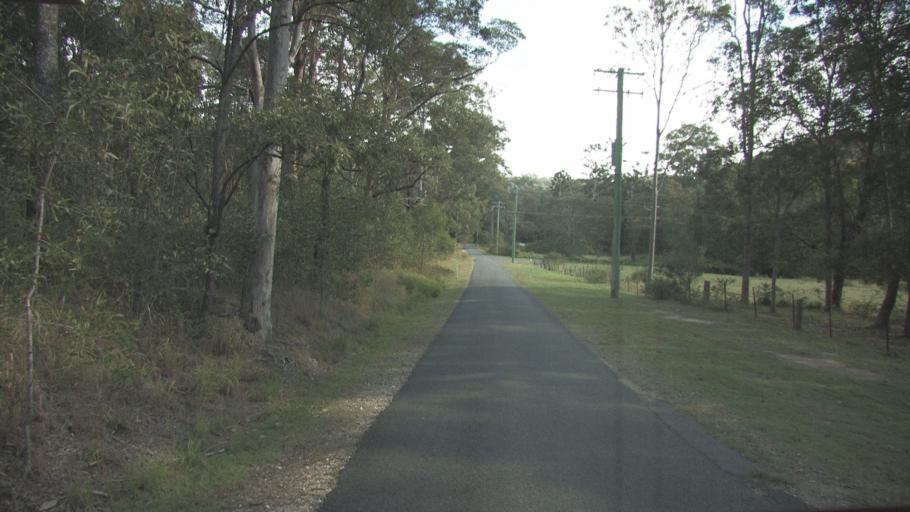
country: AU
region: Queensland
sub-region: Logan
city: Windaroo
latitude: -27.7756
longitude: 153.1771
